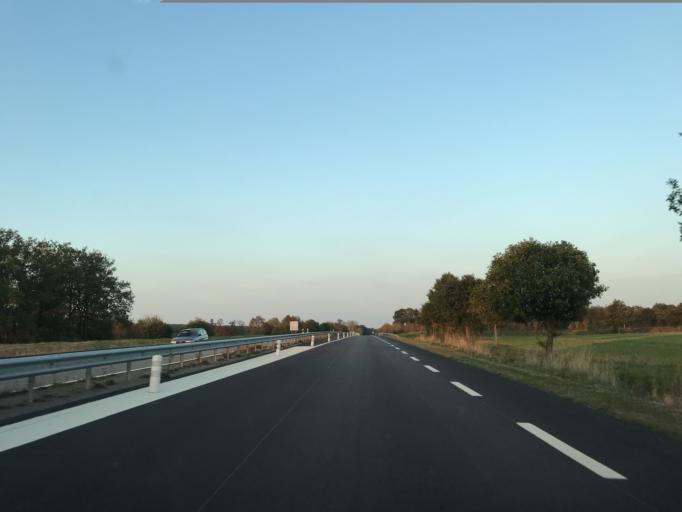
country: FR
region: Haute-Normandie
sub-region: Departement de l'Eure
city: Bourth
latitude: 48.6715
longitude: 0.7904
